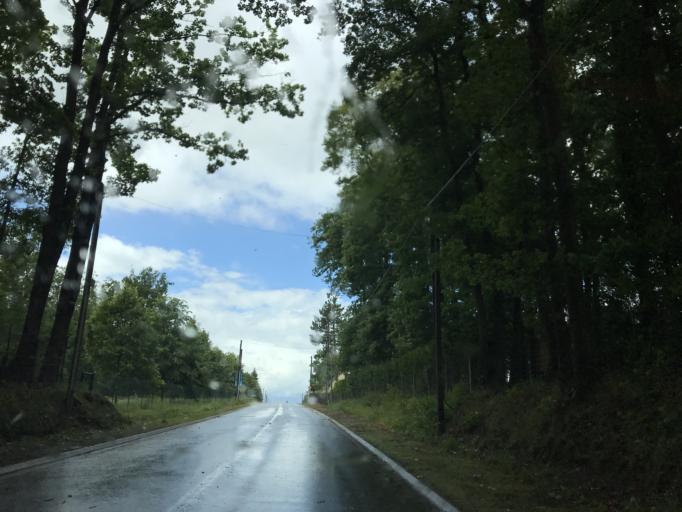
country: FR
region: Haute-Normandie
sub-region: Departement de l'Eure
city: Damville
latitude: 48.8739
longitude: 1.0666
